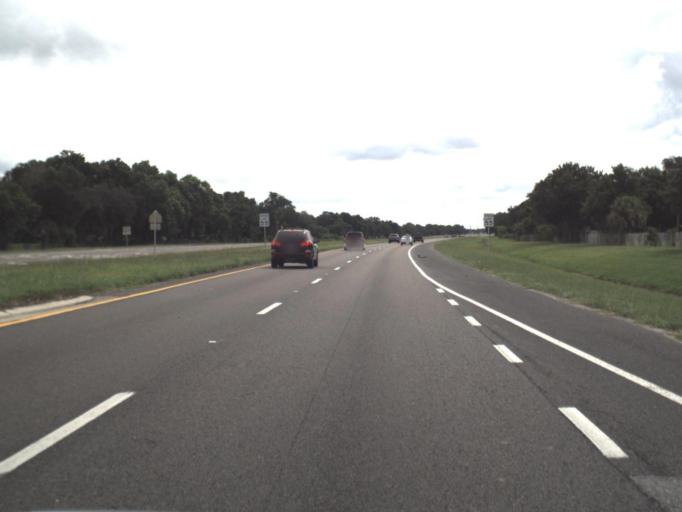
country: US
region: Florida
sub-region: Manatee County
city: Samoset
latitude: 27.4729
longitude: -82.5425
